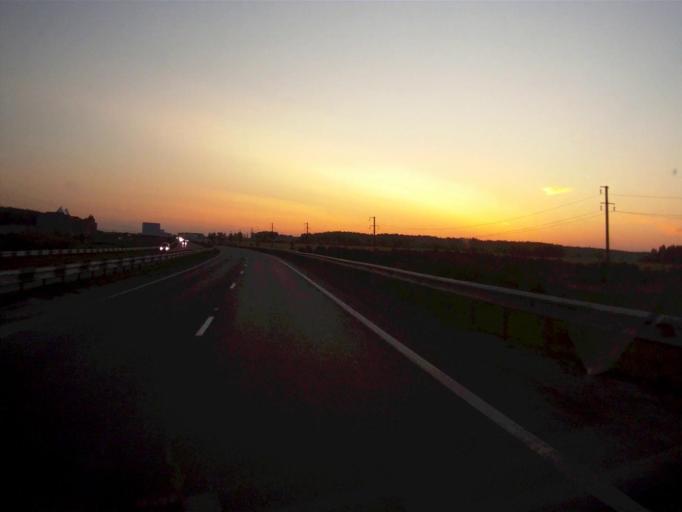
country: RU
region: Chelyabinsk
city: Roshchino
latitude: 55.1947
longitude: 61.2034
